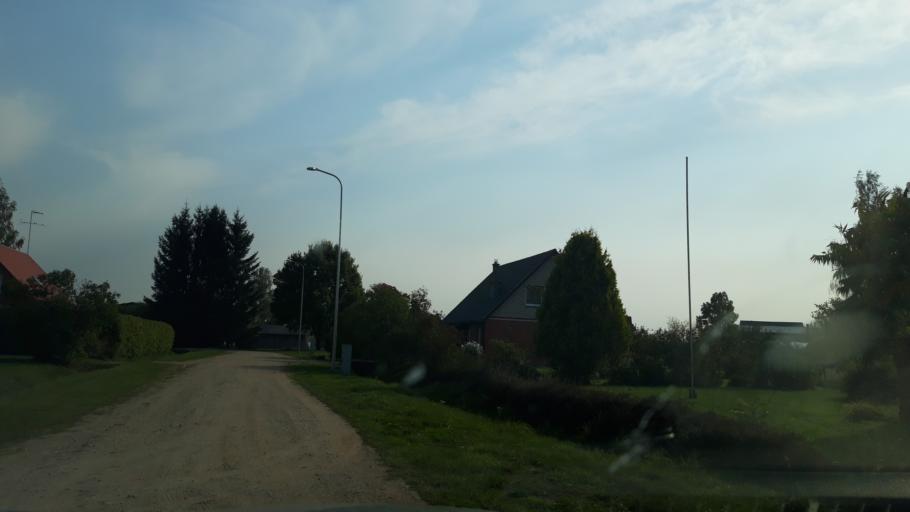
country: LV
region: Mazsalaca
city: Mazsalaca
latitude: 57.8563
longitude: 25.0397
